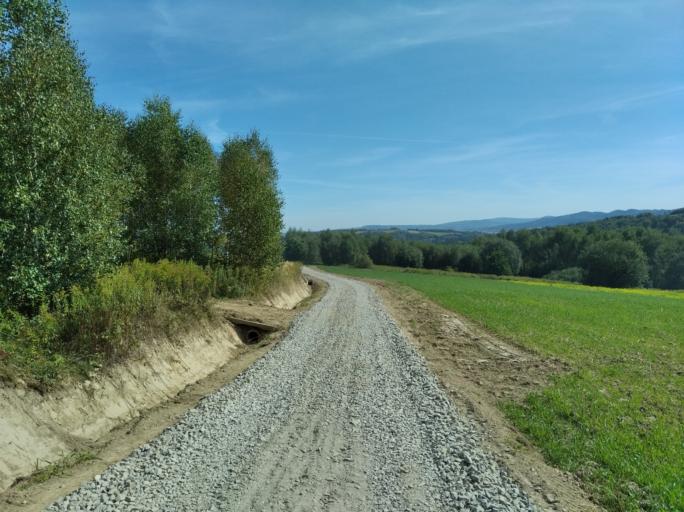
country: PL
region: Subcarpathian Voivodeship
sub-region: Powiat ropczycko-sedziszowski
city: Wielopole Skrzynskie
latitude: 49.9014
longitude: 21.6213
